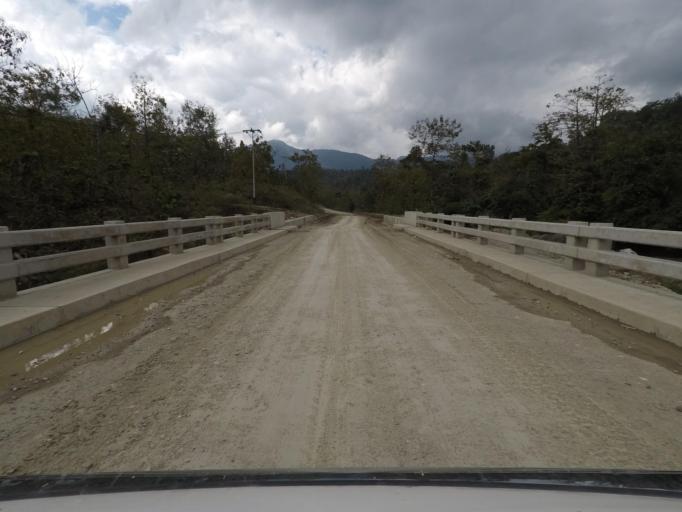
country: TL
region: Viqueque
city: Viqueque
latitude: -8.8166
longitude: 126.3801
